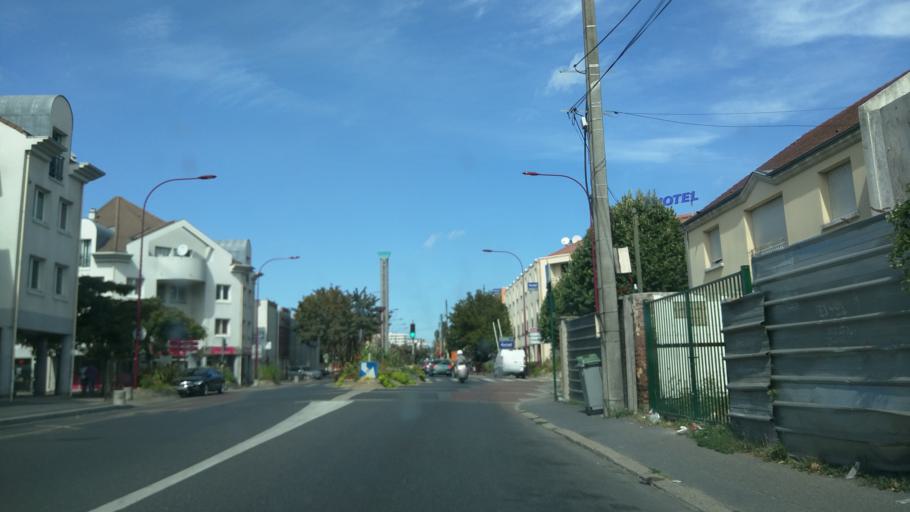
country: FR
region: Ile-de-France
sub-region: Departement du Val-d'Oise
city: Bezons
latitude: 48.9307
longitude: 2.2126
